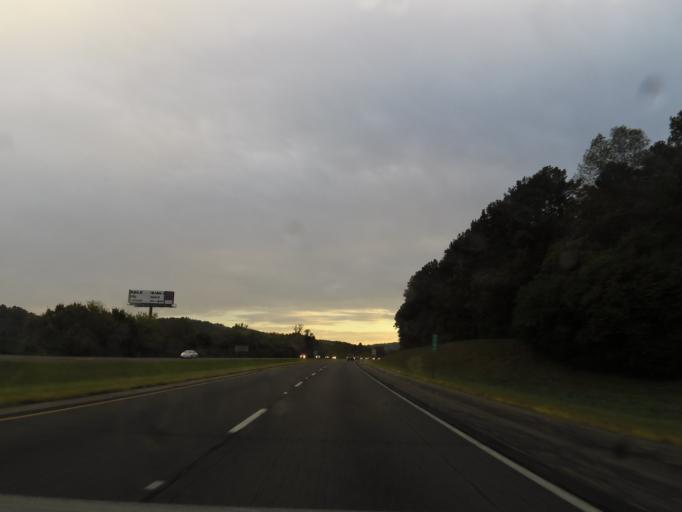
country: US
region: Alabama
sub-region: Jefferson County
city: Argo
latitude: 33.6884
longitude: -86.5310
